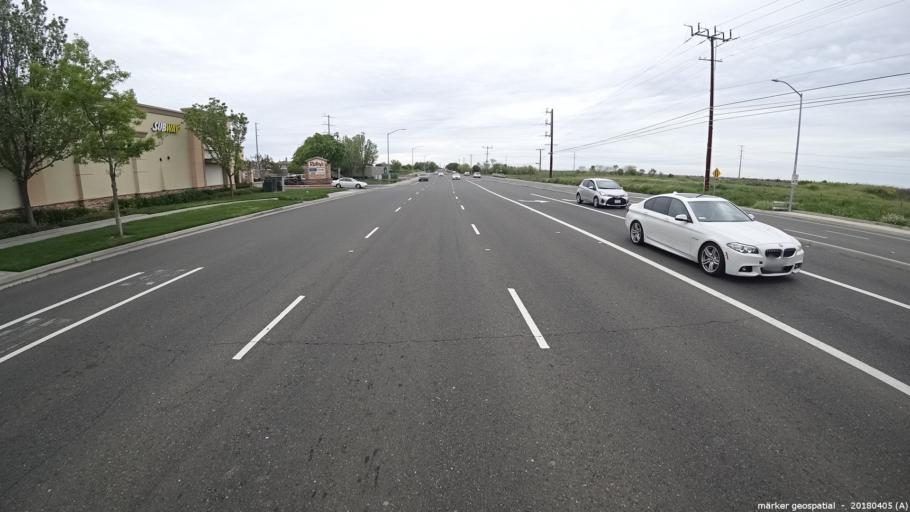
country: US
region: California
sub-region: Sacramento County
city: Laguna
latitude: 38.4080
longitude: -121.4499
